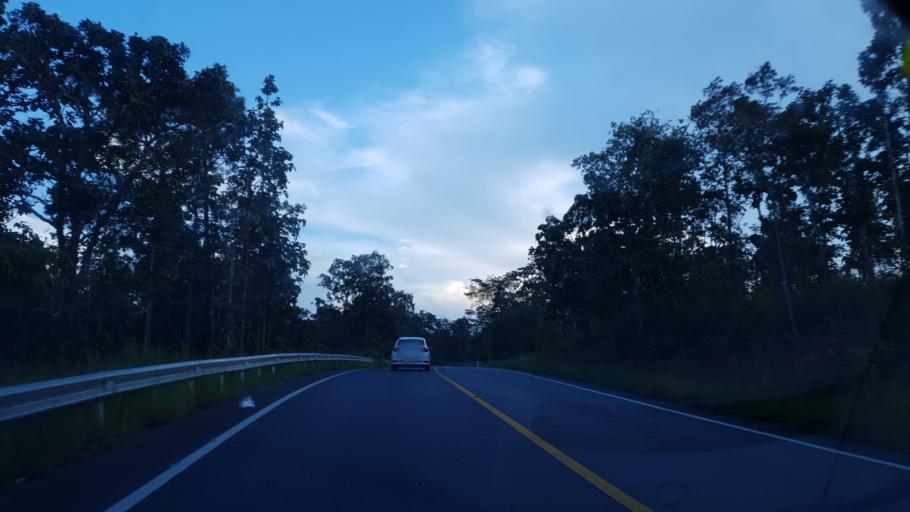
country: TH
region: Mae Hong Son
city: Khun Yuam
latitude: 18.7952
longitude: 97.9328
